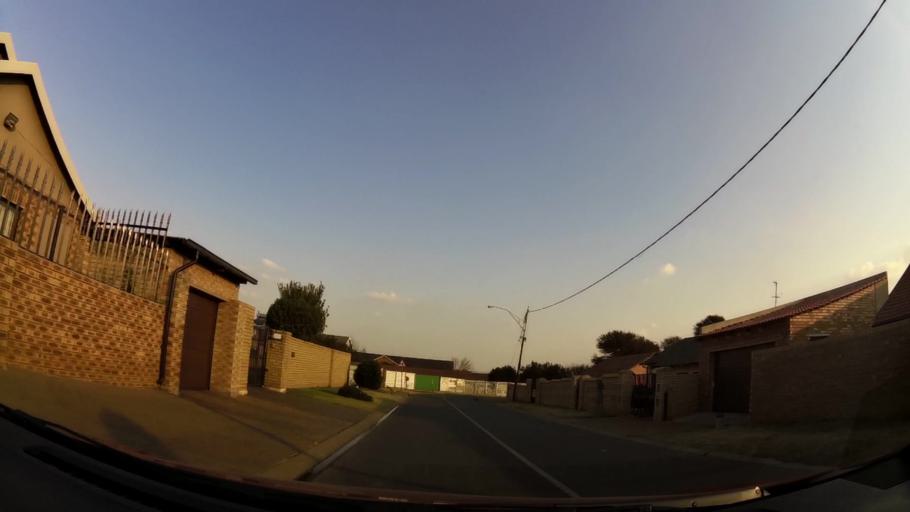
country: ZA
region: Gauteng
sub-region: City of Johannesburg Metropolitan Municipality
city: Soweto
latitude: -26.2824
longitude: 27.8978
